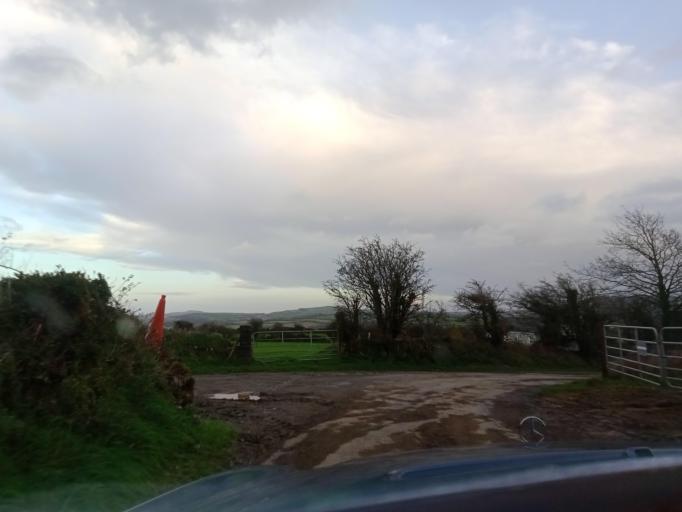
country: IE
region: Leinster
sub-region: Loch Garman
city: New Ross
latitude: 52.3476
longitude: -7.0118
